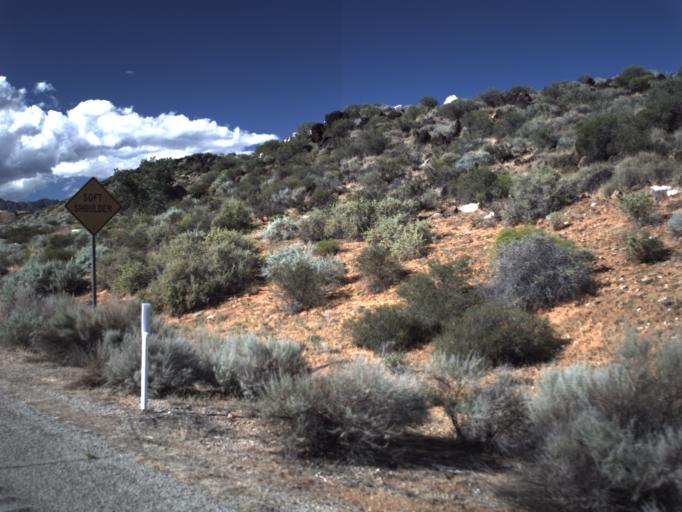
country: US
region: Utah
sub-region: Washington County
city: Toquerville
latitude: 37.2601
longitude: -113.2935
